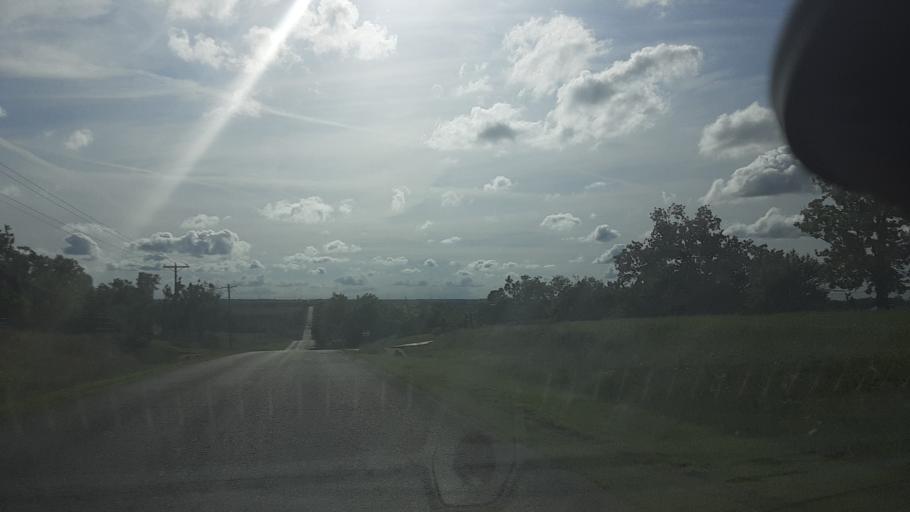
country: US
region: Oklahoma
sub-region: Logan County
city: Langston
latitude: 36.0578
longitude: -97.3821
